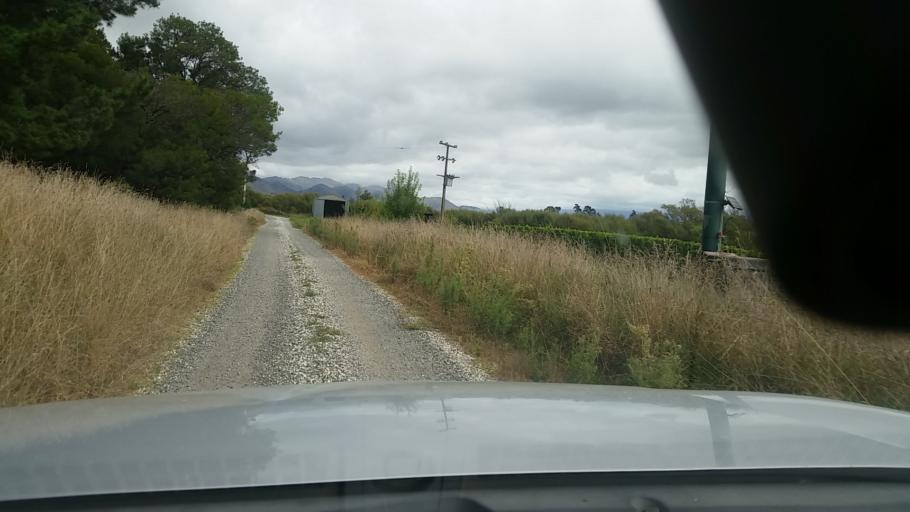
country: NZ
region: Marlborough
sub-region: Marlborough District
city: Blenheim
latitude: -41.6935
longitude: 174.1254
